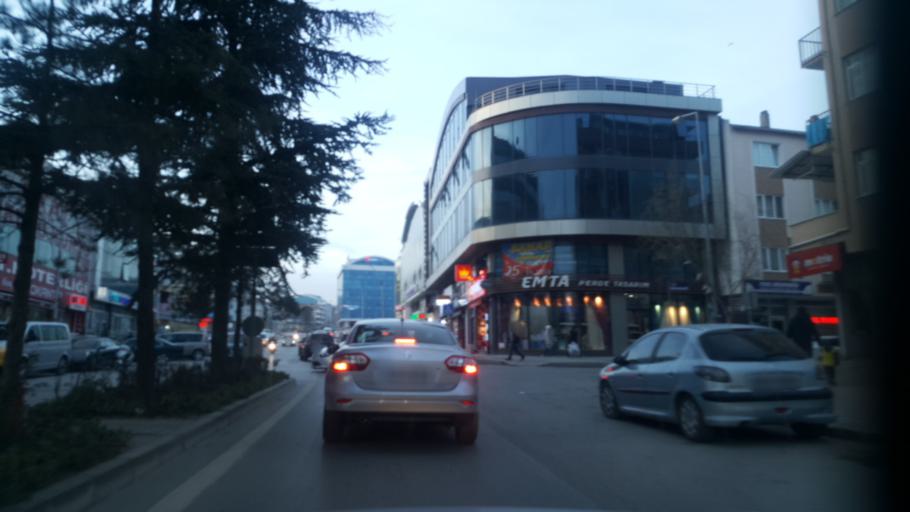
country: TR
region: Kocaeli
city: Gebze
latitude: 40.7933
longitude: 29.4336
